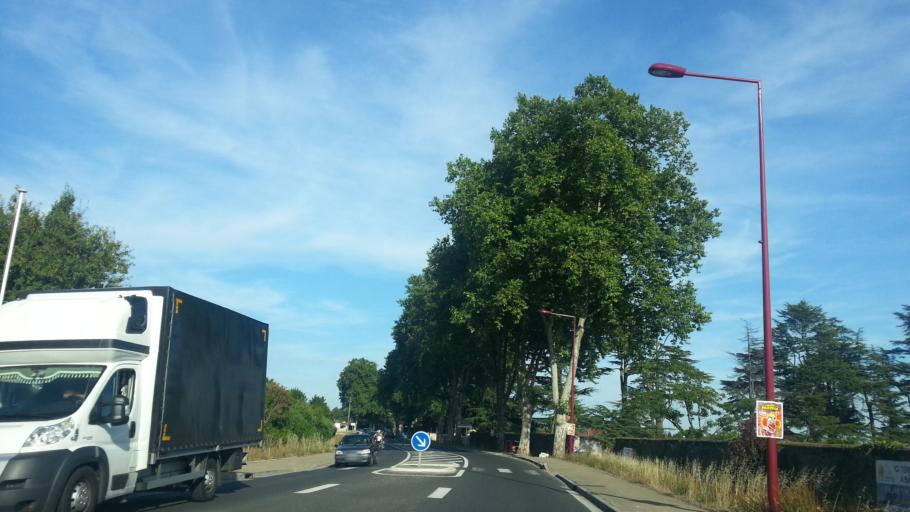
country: FR
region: Aquitaine
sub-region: Departement de la Gironde
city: Castres-Gironde
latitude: 44.6962
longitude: -0.4430
